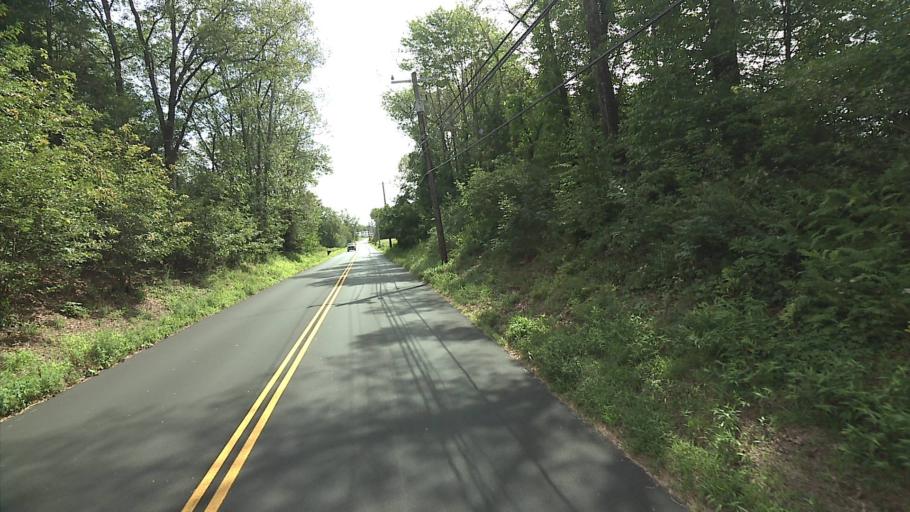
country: US
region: Connecticut
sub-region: Windham County
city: South Woodstock
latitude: 41.9389
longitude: -71.9961
